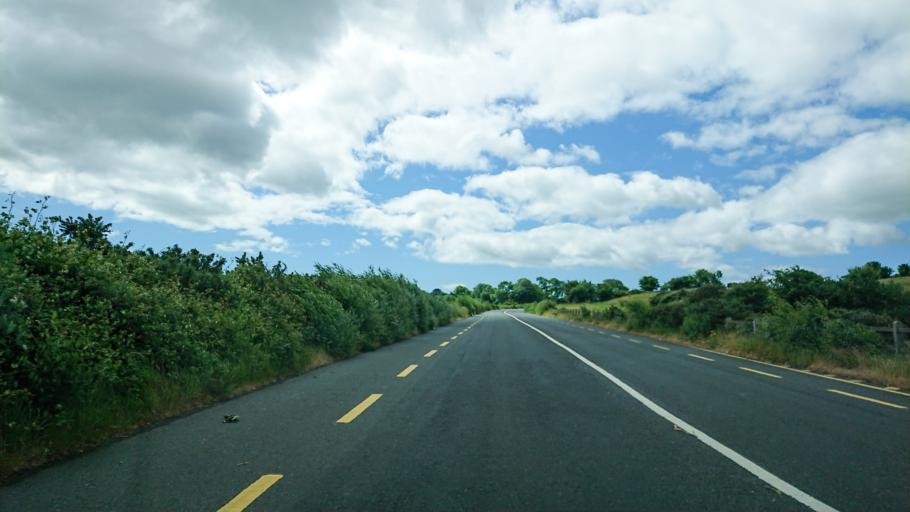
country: IE
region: Munster
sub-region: Waterford
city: Tra Mhor
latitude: 52.2124
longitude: -7.1938
